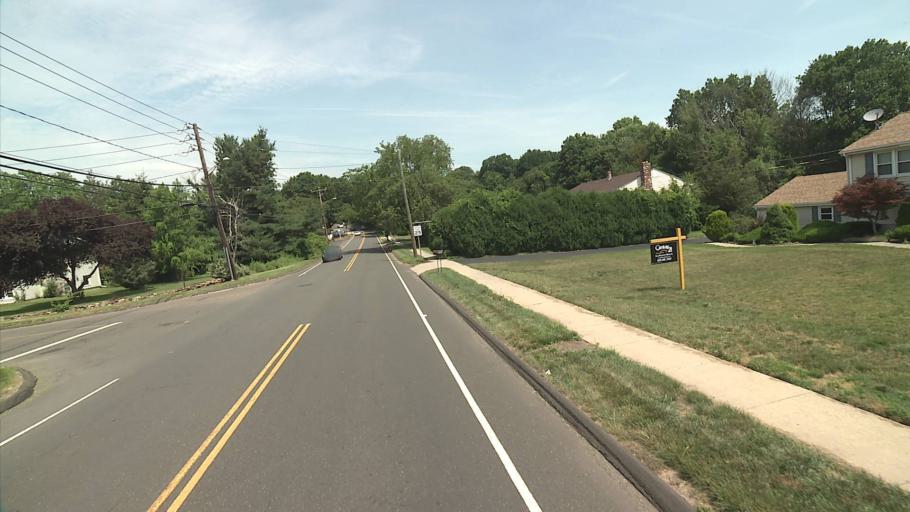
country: US
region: Connecticut
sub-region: New Haven County
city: Branford
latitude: 41.3065
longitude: -72.8195
